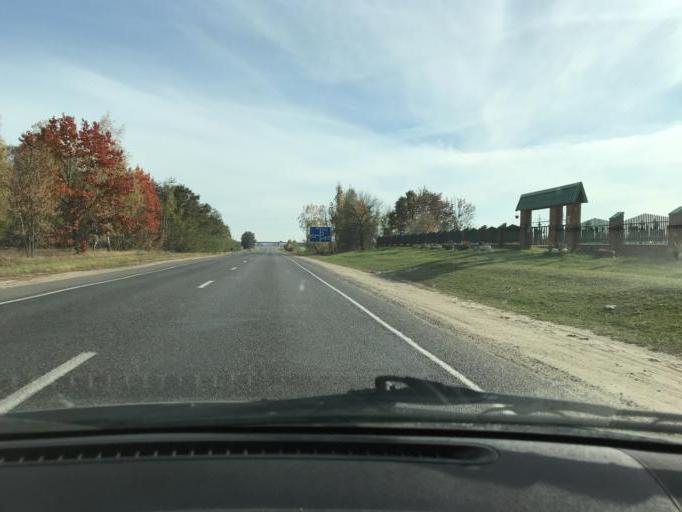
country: BY
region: Brest
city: Asnyezhytsy
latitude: 52.1920
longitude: 26.0731
